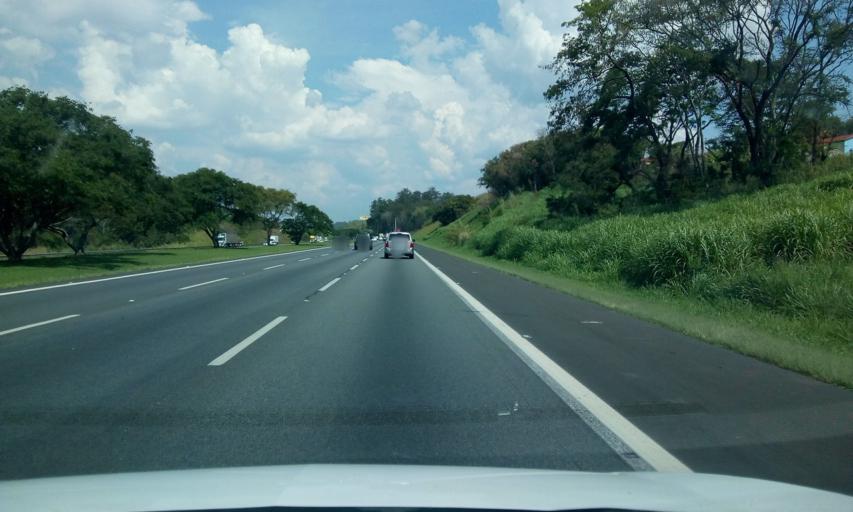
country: BR
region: Sao Paulo
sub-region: Vinhedo
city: Vinhedo
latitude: -23.0768
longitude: -47.0274
